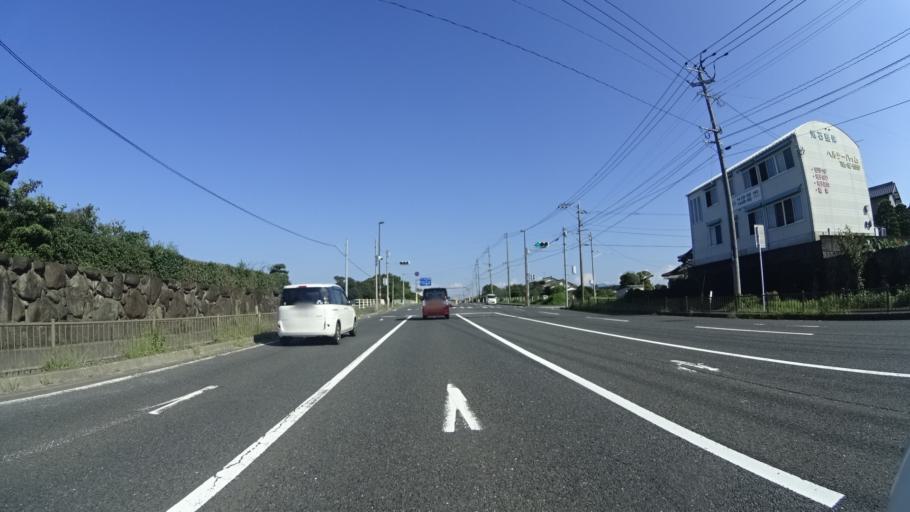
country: JP
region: Fukuoka
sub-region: Buzen-shi
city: Buzen
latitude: 33.6035
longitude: 131.1231
